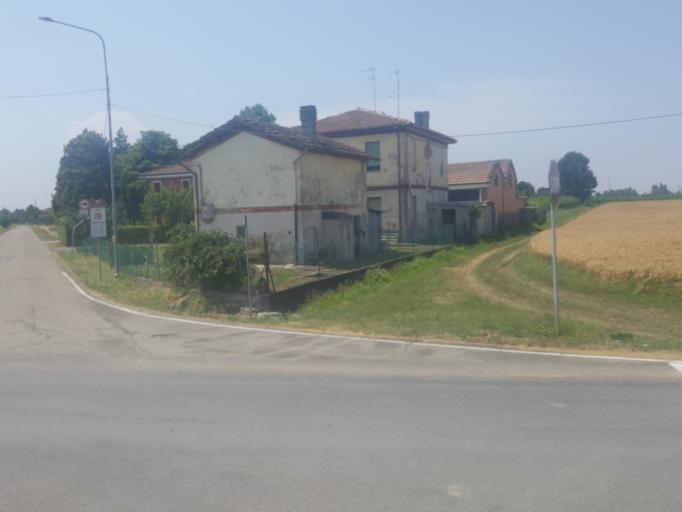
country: IT
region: Emilia-Romagna
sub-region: Provincia di Modena
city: Manzolino
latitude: 44.6042
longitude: 11.0853
